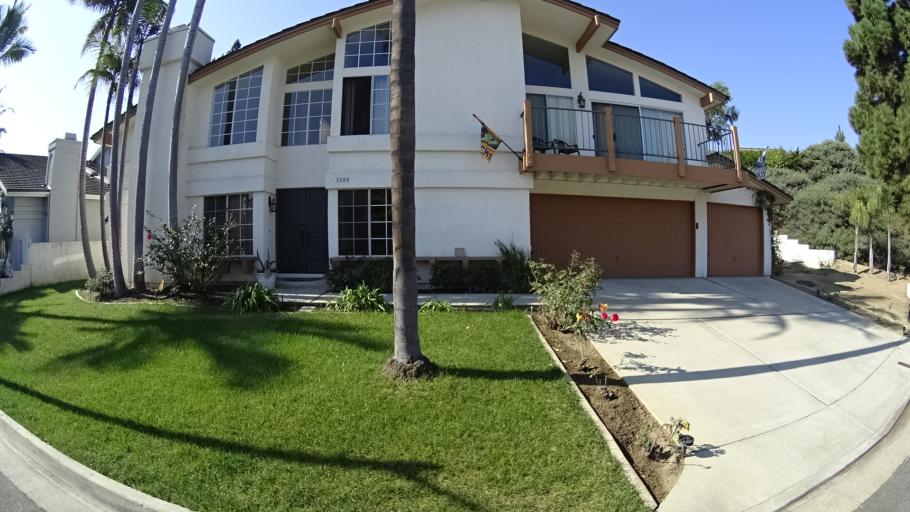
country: US
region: California
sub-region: Orange County
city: San Clemente
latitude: 33.4539
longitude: -117.6498
